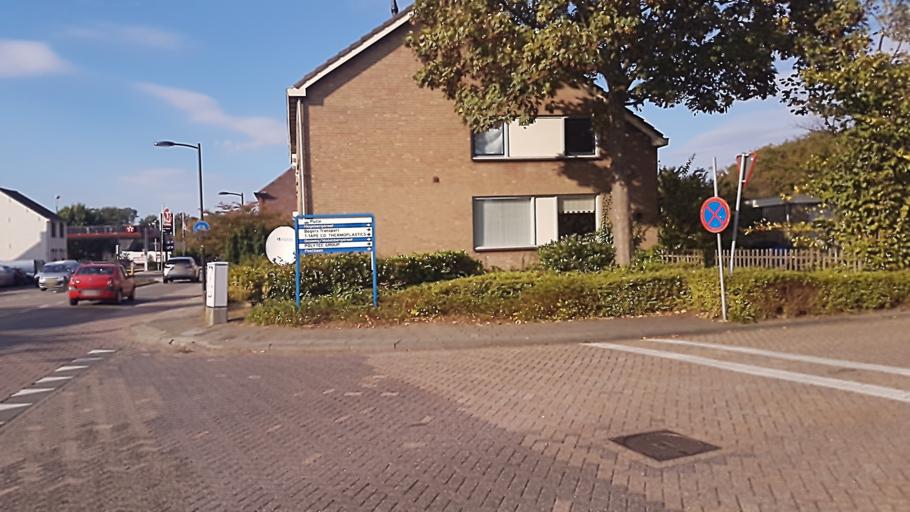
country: BE
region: Flanders
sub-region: Provincie Antwerpen
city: Stabroek
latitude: 51.3632
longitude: 4.3918
